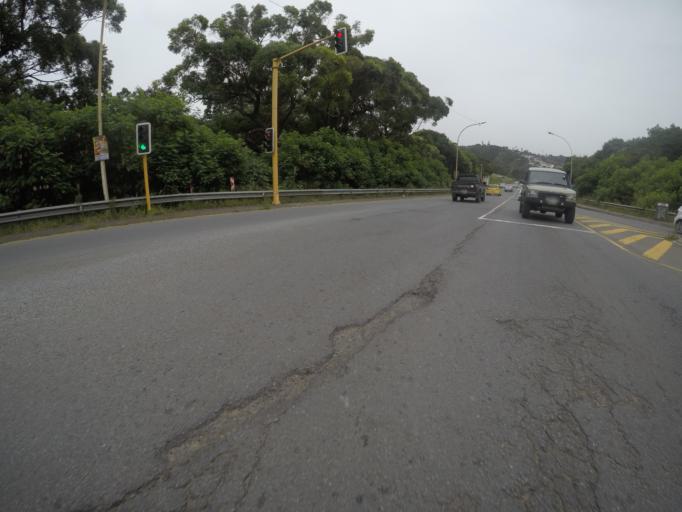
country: ZA
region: Eastern Cape
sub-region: Buffalo City Metropolitan Municipality
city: East London
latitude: -32.9754
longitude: 27.9217
